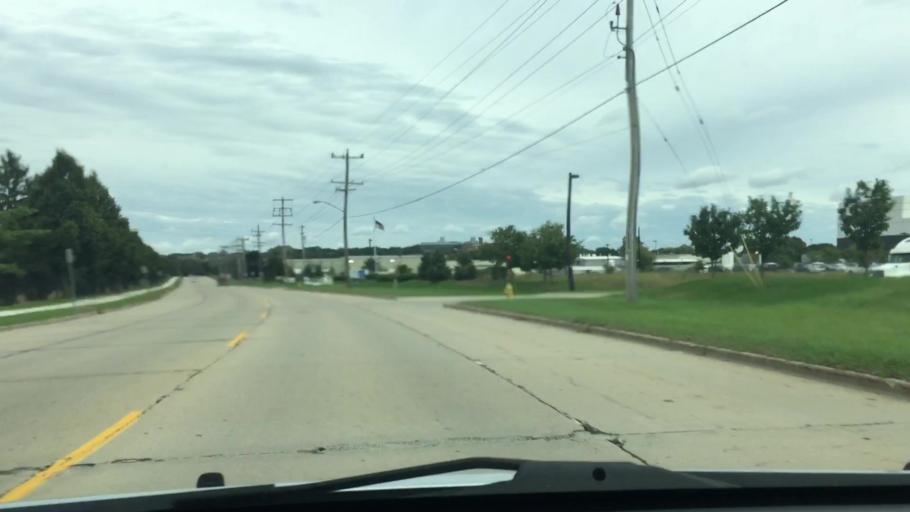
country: US
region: Wisconsin
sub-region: Waukesha County
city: Waukesha
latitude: 42.9958
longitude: -88.2491
